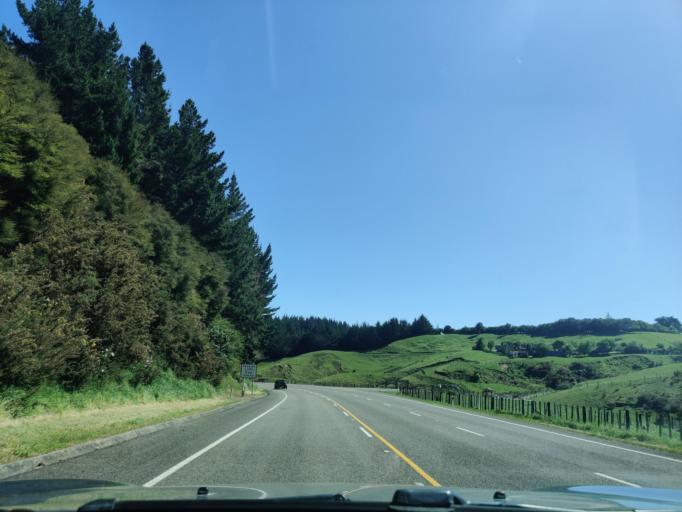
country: NZ
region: Manawatu-Wanganui
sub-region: Wanganui District
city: Wanganui
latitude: -39.8347
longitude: 174.9091
